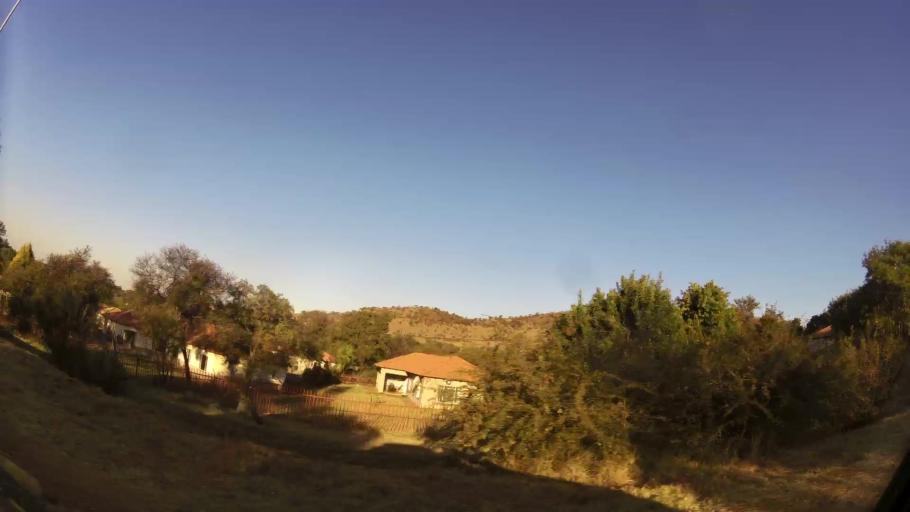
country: ZA
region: North-West
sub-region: Bojanala Platinum District Municipality
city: Rustenburg
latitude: -25.7156
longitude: 27.2391
